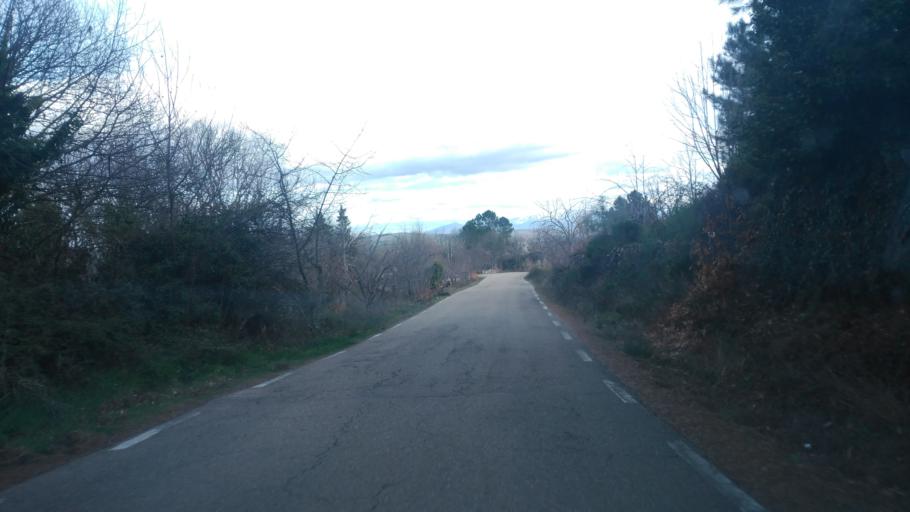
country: ES
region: Castille and Leon
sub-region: Provincia de Salamanca
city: Mogarraz
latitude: 40.4939
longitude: -6.0448
